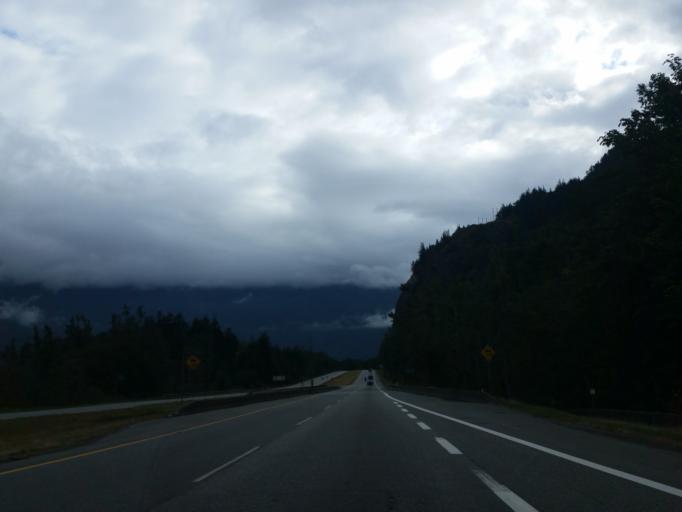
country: CA
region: British Columbia
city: Hope
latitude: 49.3569
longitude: -121.5756
